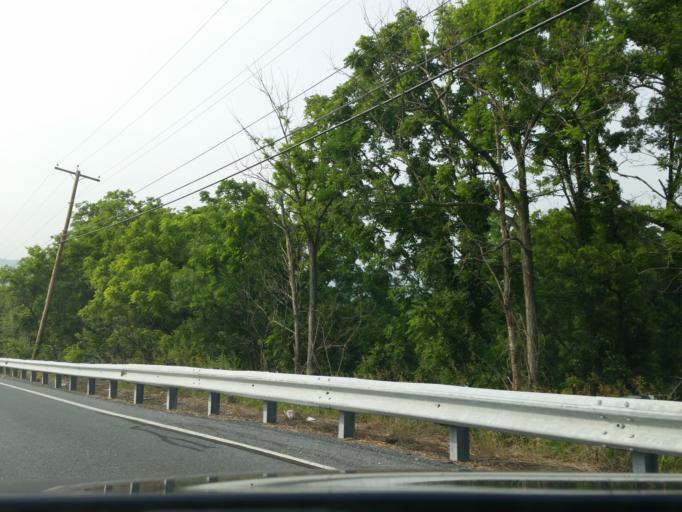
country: US
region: Pennsylvania
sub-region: Lebanon County
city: Palmyra
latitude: 40.4075
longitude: -76.6008
